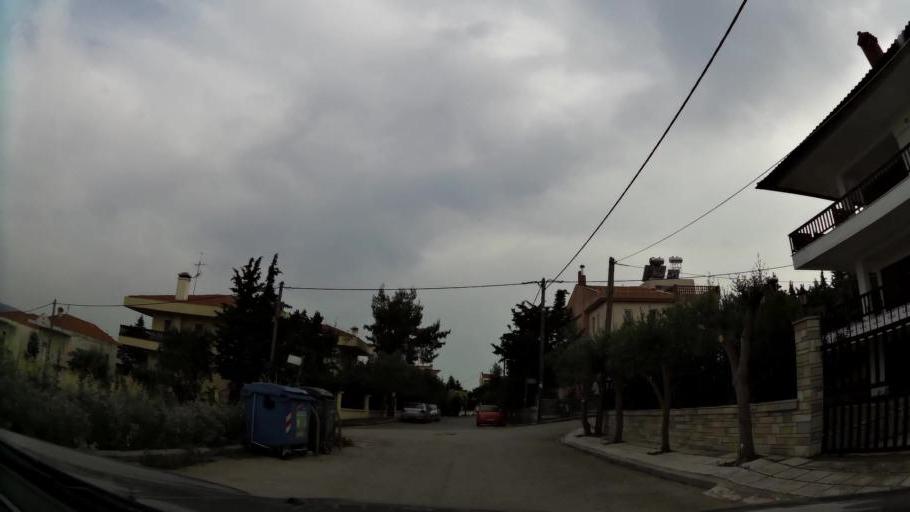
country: GR
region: Central Macedonia
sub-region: Nomos Thessalonikis
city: Oraiokastro
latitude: 40.7126
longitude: 22.9320
